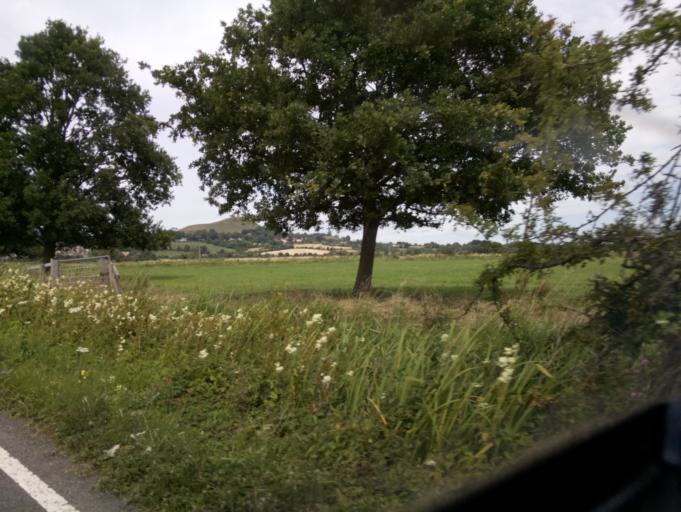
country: GB
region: England
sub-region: Somerset
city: Glastonbury
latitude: 51.1296
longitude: -2.7123
